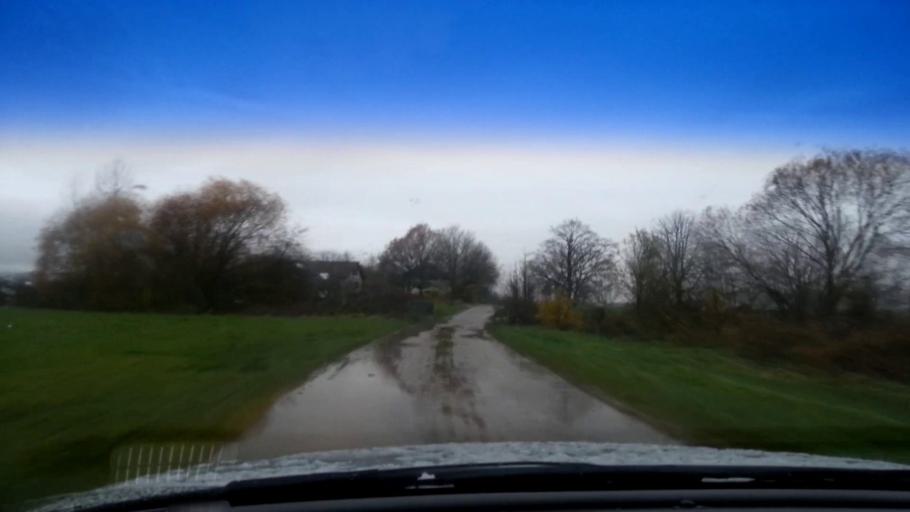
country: DE
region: Bavaria
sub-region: Upper Franconia
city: Viereth-Trunstadt
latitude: 49.9310
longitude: 10.7899
